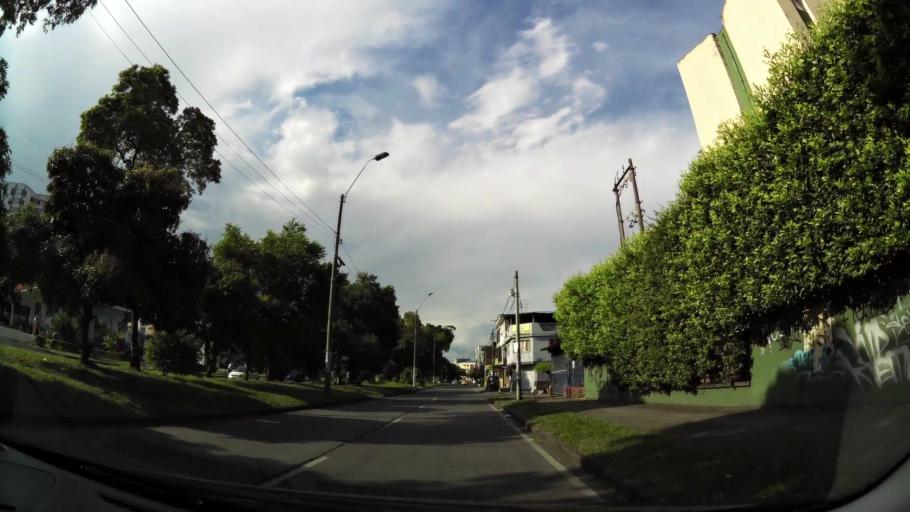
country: CO
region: Valle del Cauca
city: Cali
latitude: 3.4270
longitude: -76.5277
